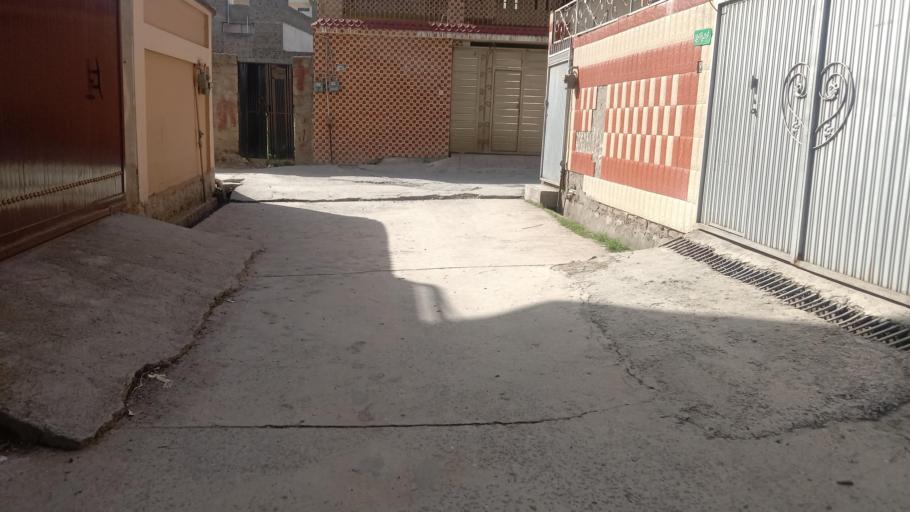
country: PK
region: Khyber Pakhtunkhwa
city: Abbottabad
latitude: 34.1792
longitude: 73.2242
